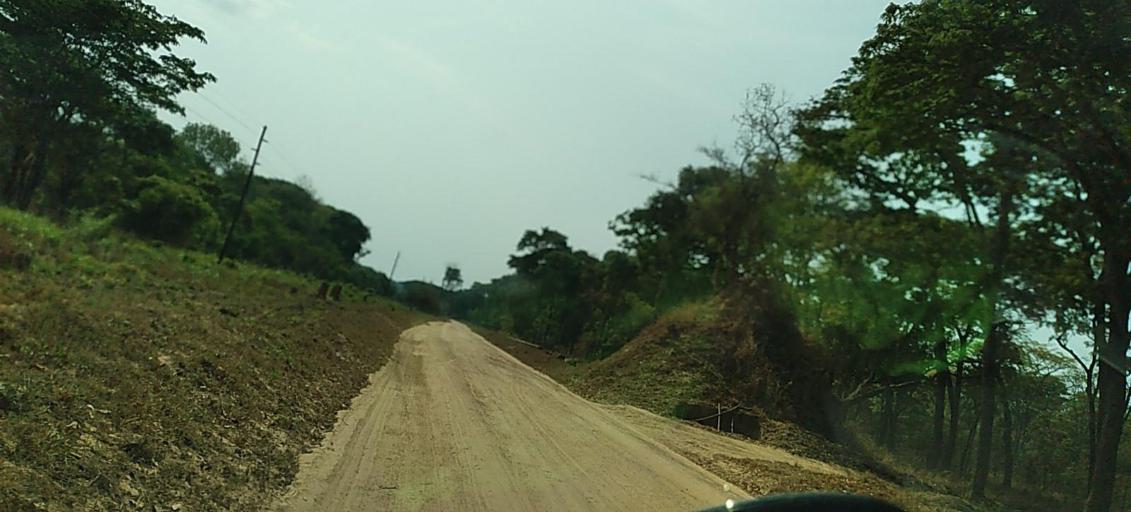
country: ZM
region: North-Western
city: Solwezi
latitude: -12.6991
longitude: 26.4123
